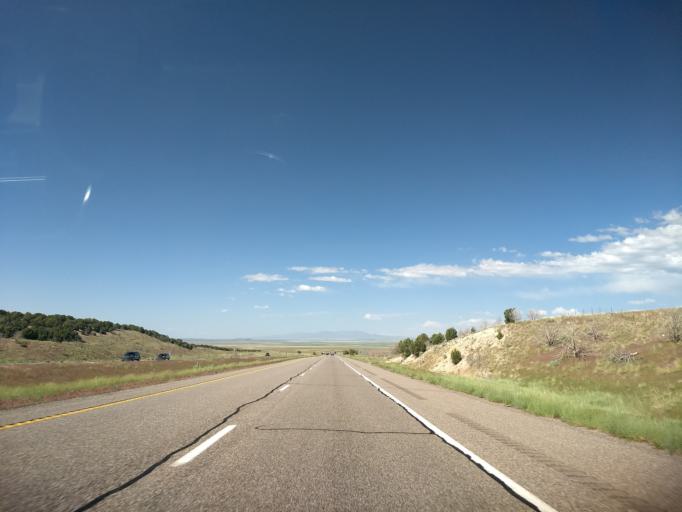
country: US
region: Utah
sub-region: Millard County
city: Fillmore
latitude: 38.7234
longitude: -112.5955
